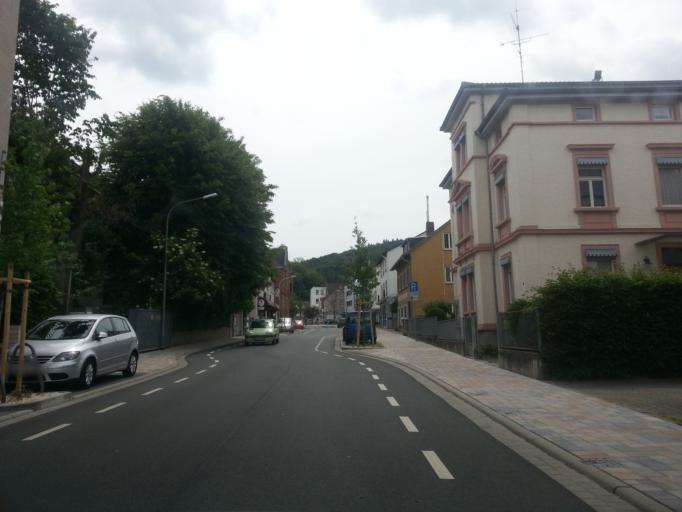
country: DE
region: Hesse
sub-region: Regierungsbezirk Darmstadt
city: Seeheim-Jugenheim
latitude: 49.7552
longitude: 8.6365
